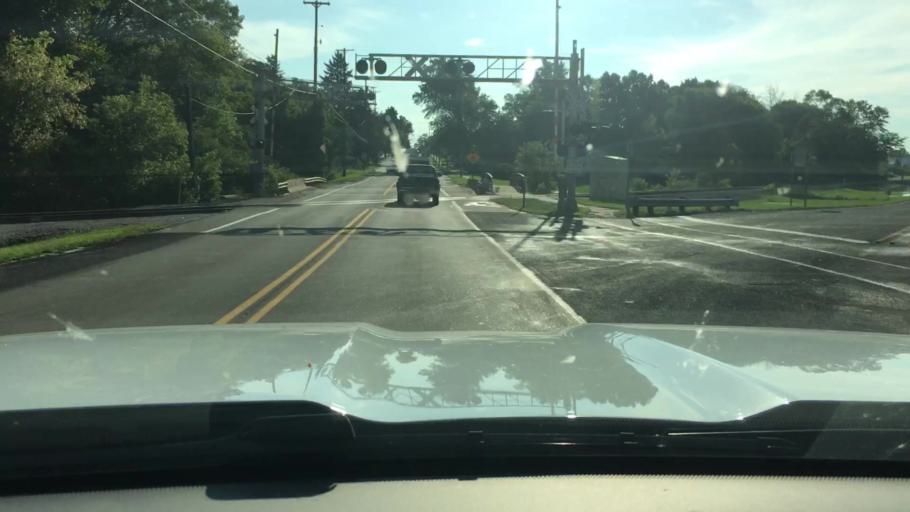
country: US
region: Michigan
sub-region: Kent County
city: Kent City
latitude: 43.2195
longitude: -85.7559
